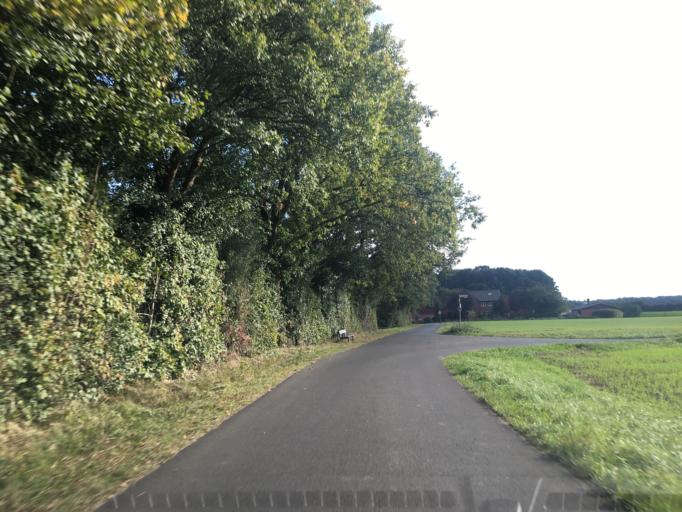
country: DE
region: North Rhine-Westphalia
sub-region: Regierungsbezirk Munster
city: Senden
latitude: 51.9513
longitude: 7.5176
